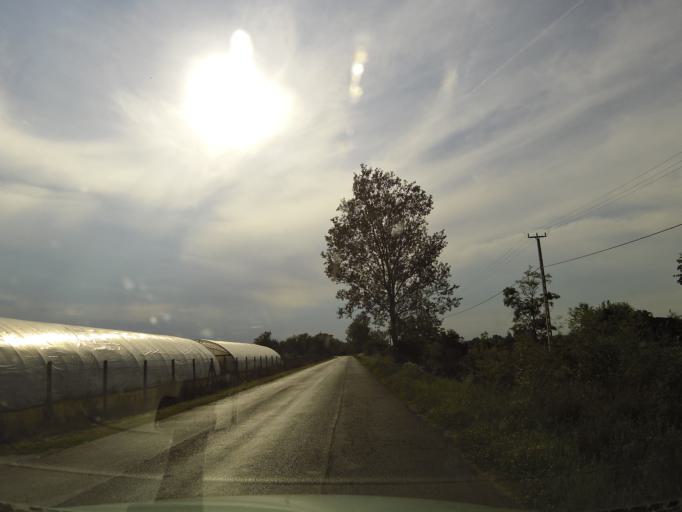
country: HU
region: Csongrad
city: Balastya
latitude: 46.4366
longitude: 19.9769
